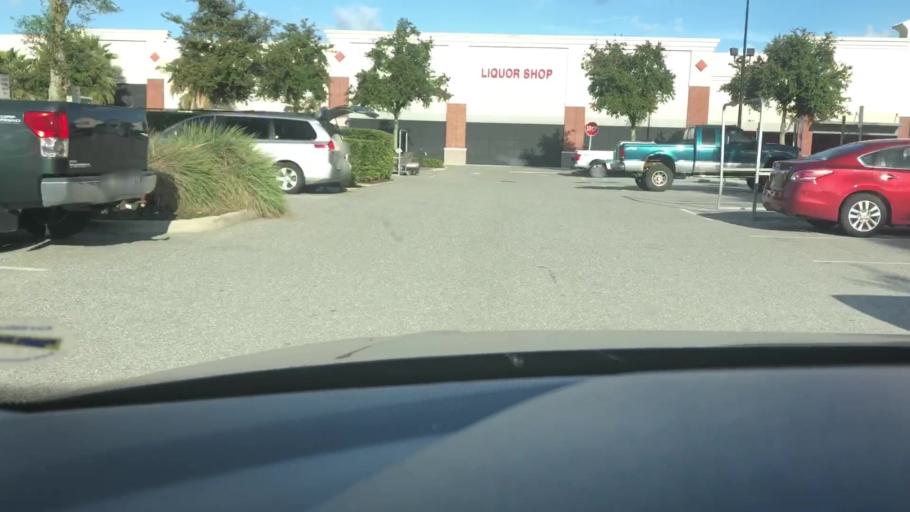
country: US
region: Florida
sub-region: Volusia County
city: Port Orange
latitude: 29.1090
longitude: -81.0249
